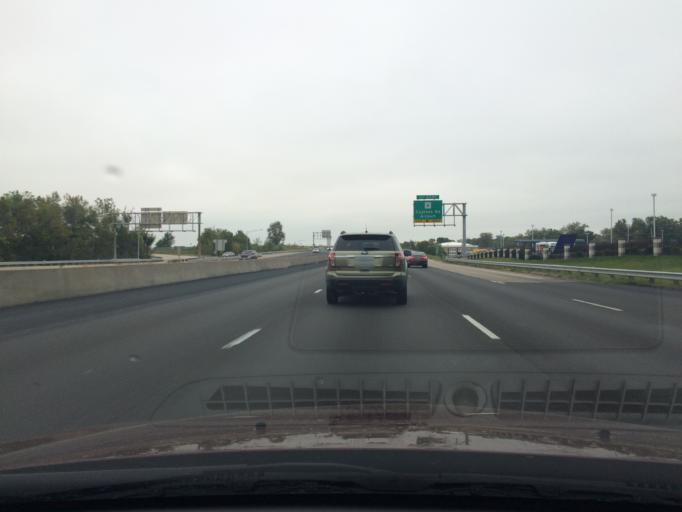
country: US
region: Missouri
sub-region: Saint Louis County
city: Saint Ann
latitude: 38.7431
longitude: -90.3897
